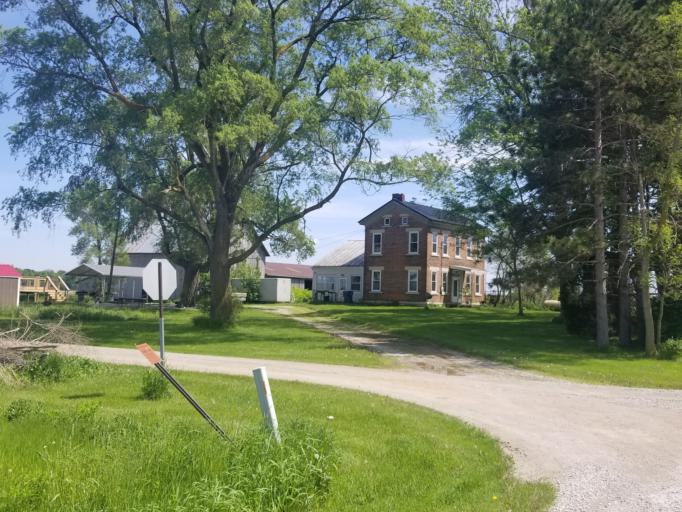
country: US
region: Ohio
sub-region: Huron County
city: Willard
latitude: 41.0518
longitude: -82.9388
